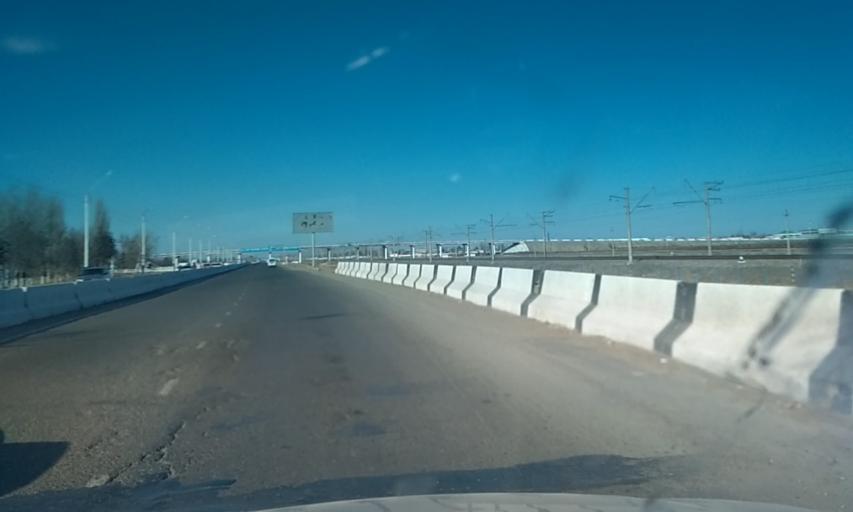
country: UZ
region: Sirdaryo
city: Guliston
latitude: 40.4699
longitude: 68.7719
